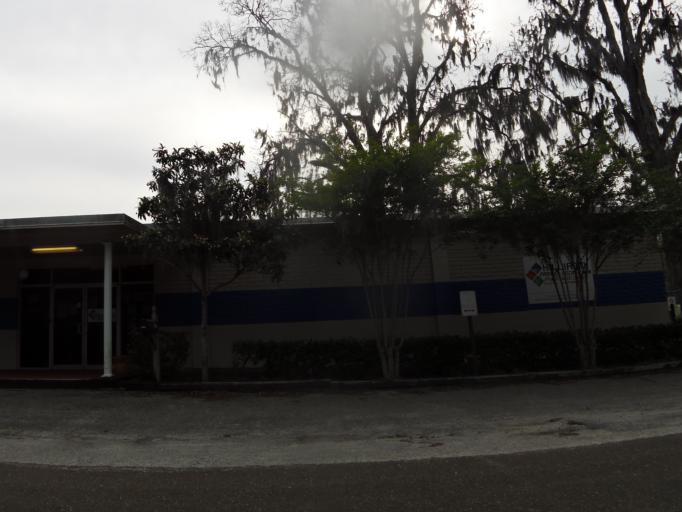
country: US
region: Florida
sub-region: Nassau County
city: Hilliard
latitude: 30.6924
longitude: -81.9236
